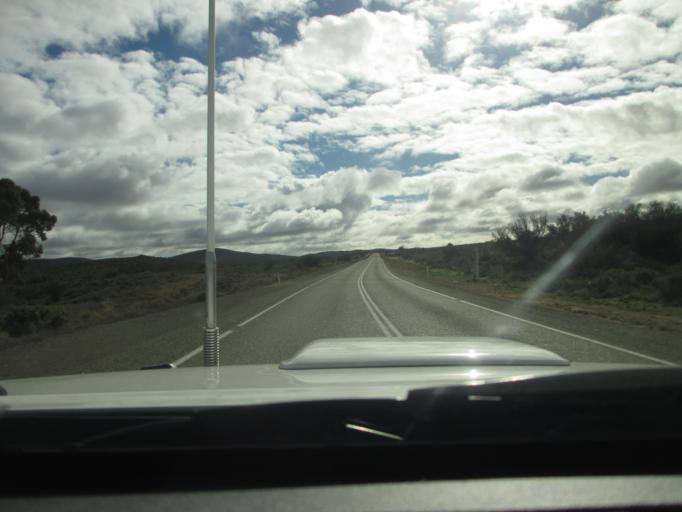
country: AU
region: South Australia
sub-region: Flinders Ranges
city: Quorn
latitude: -32.2312
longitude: 138.5146
